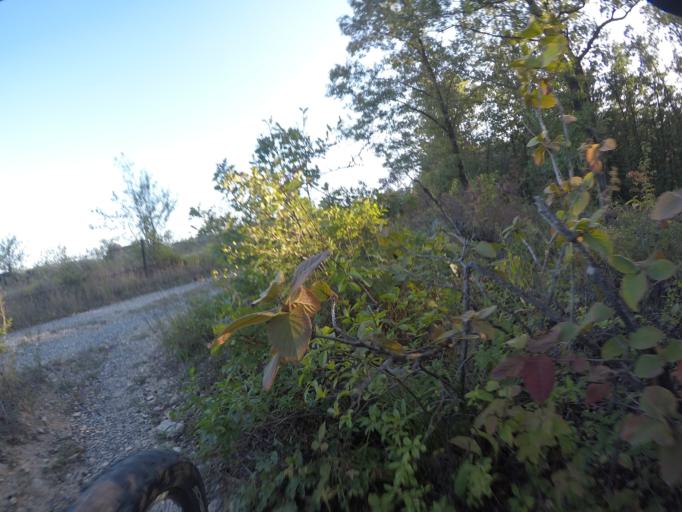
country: AT
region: Lower Austria
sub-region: Politischer Bezirk Bruck an der Leitha
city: Mannersdorf am Leithagebirge
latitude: 47.9624
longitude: 16.6017
